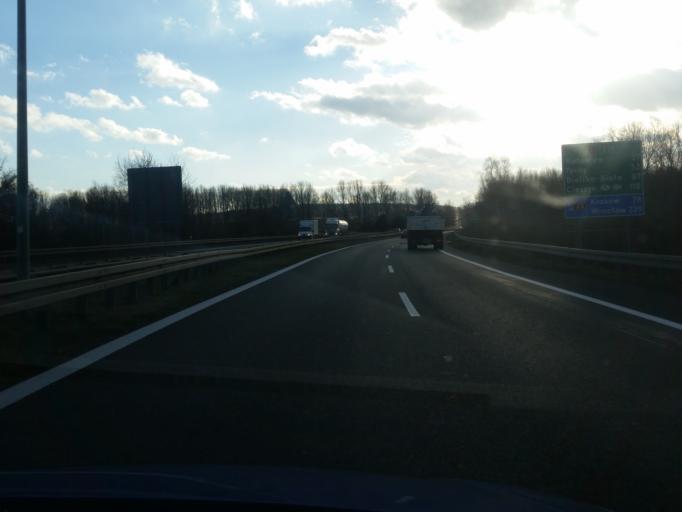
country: PL
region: Silesian Voivodeship
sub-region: Powiat bedzinski
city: Siewierz
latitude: 50.4533
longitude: 19.2293
